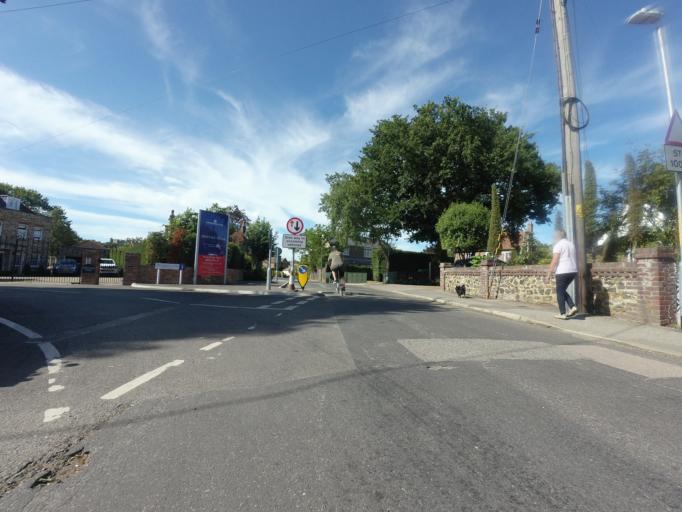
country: GB
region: England
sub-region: Kent
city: Birchington-on-Sea
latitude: 51.3523
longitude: 1.2543
